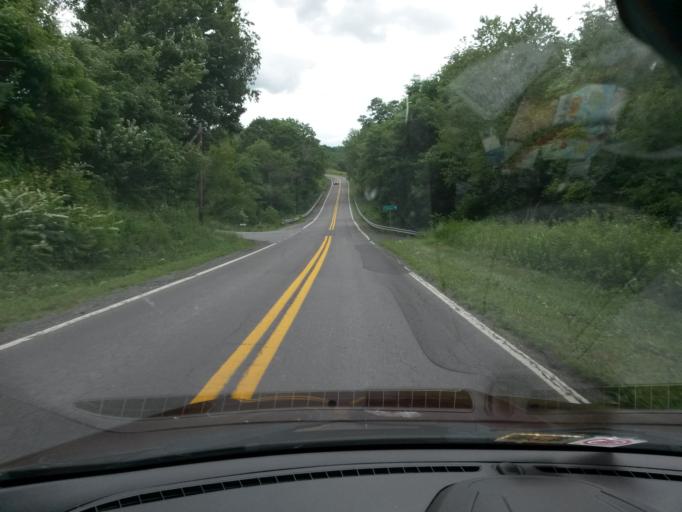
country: US
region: West Virginia
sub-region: Monroe County
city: Union
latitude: 37.5857
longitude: -80.4562
